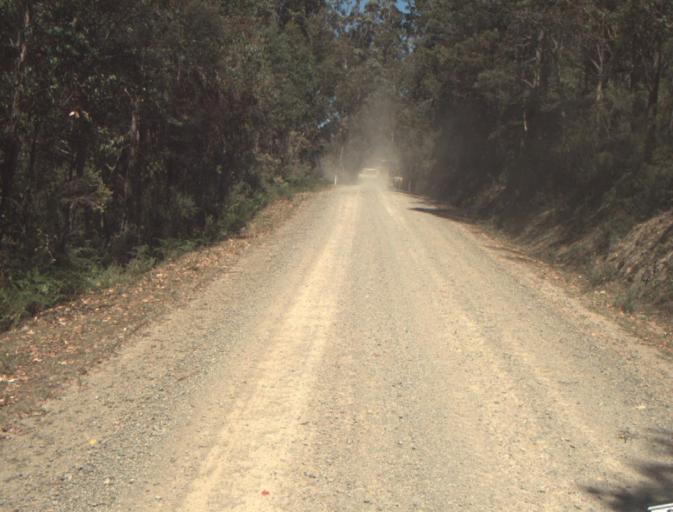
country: AU
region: Tasmania
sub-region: Dorset
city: Scottsdale
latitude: -41.3906
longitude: 147.5097
